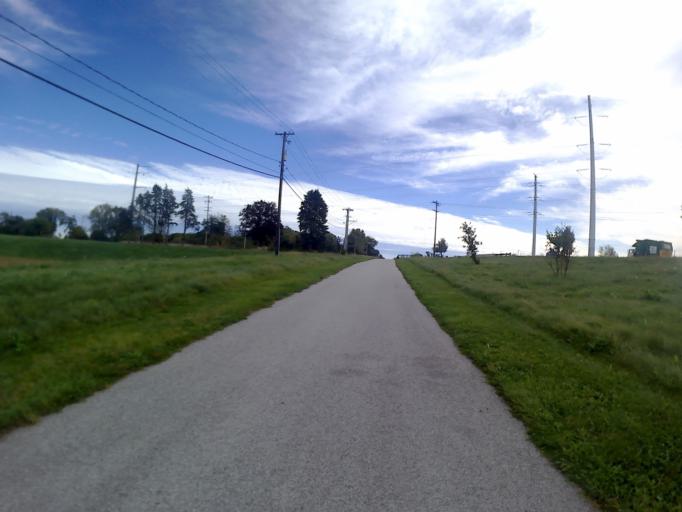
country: US
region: Illinois
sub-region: Kane County
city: South Elgin
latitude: 41.9768
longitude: -88.2679
